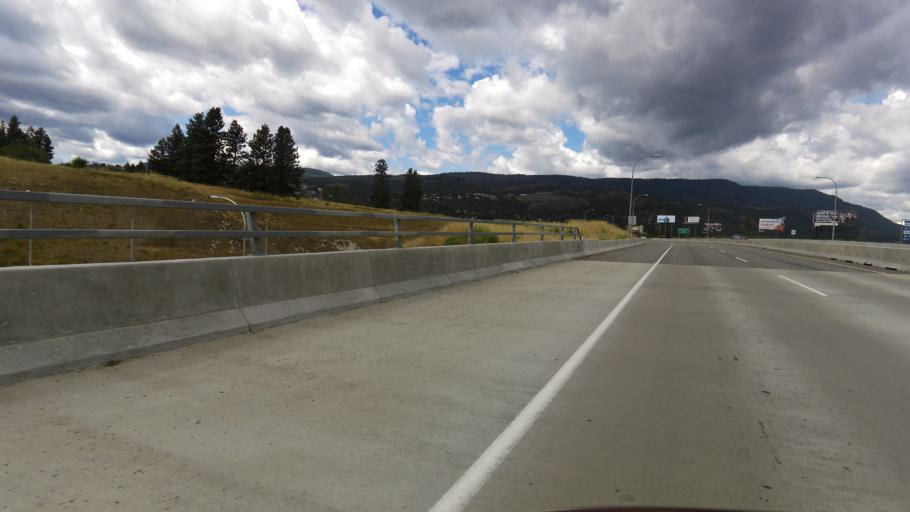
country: CA
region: British Columbia
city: Kelowna
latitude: 49.8840
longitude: -119.5265
